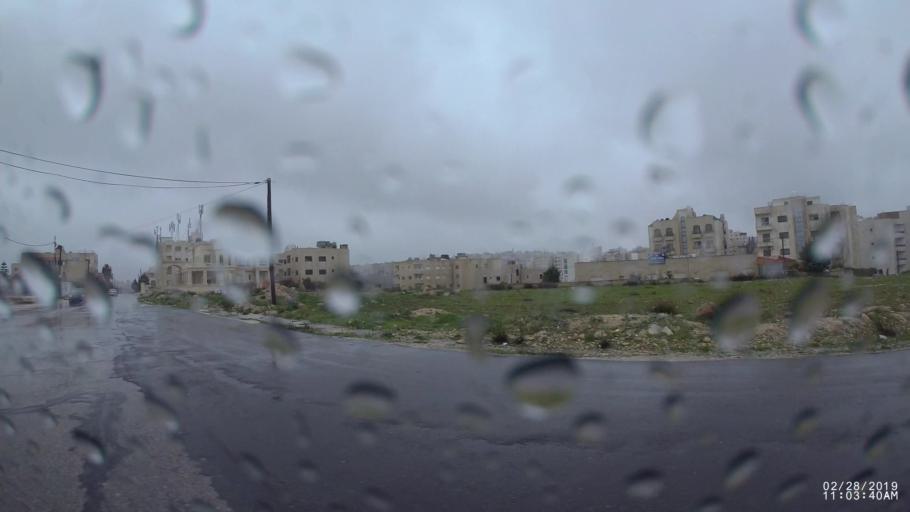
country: JO
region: Amman
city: Al Jubayhah
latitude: 32.0141
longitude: 35.8949
